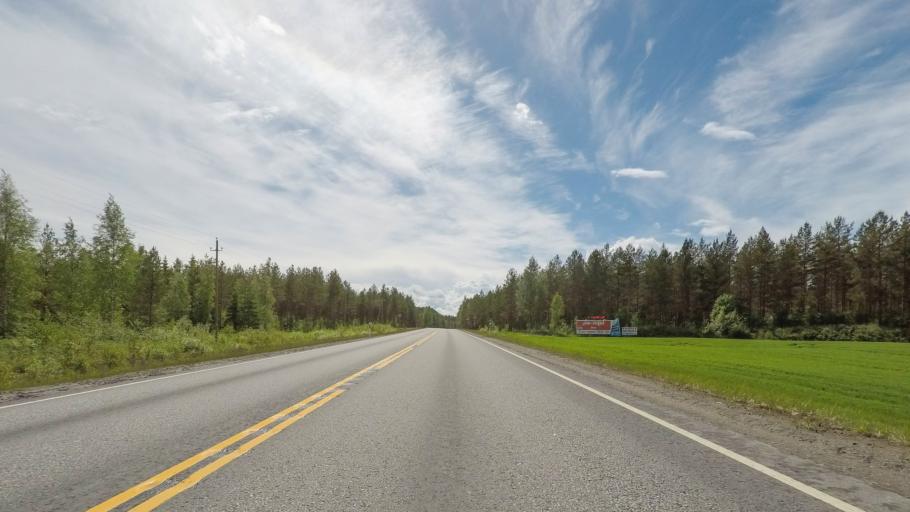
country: FI
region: Central Finland
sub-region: Jyvaeskylae
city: Hankasalmi
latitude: 62.3763
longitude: 26.5893
